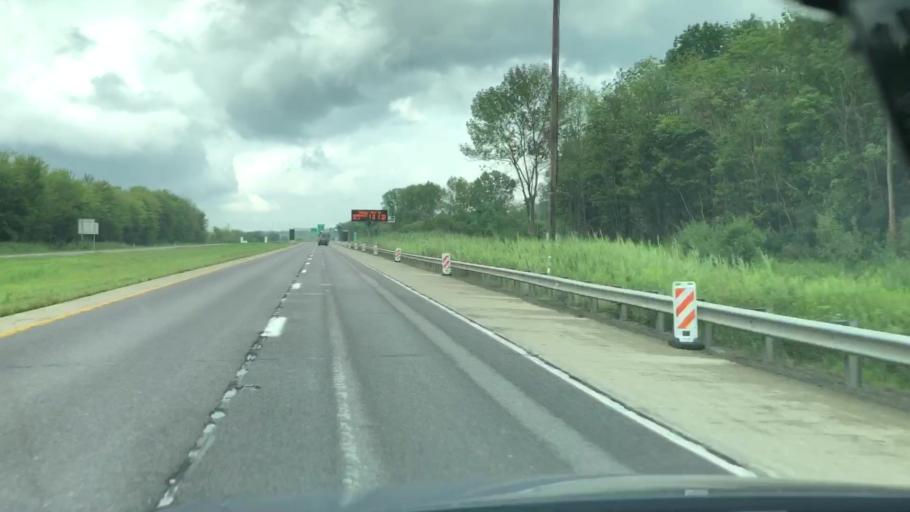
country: US
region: Pennsylvania
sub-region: Erie County
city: Fairview
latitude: 42.0170
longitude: -80.1395
